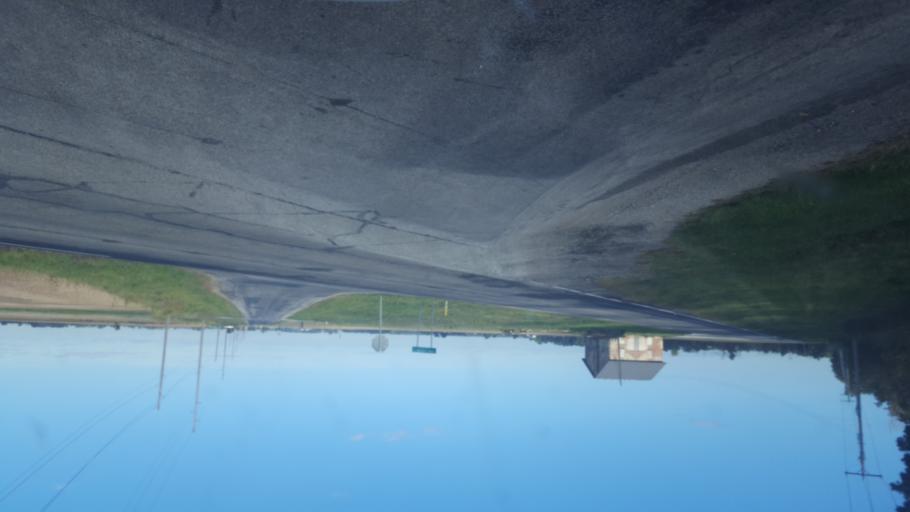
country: US
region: Ohio
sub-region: Marion County
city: Marion
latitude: 40.6884
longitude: -83.0909
